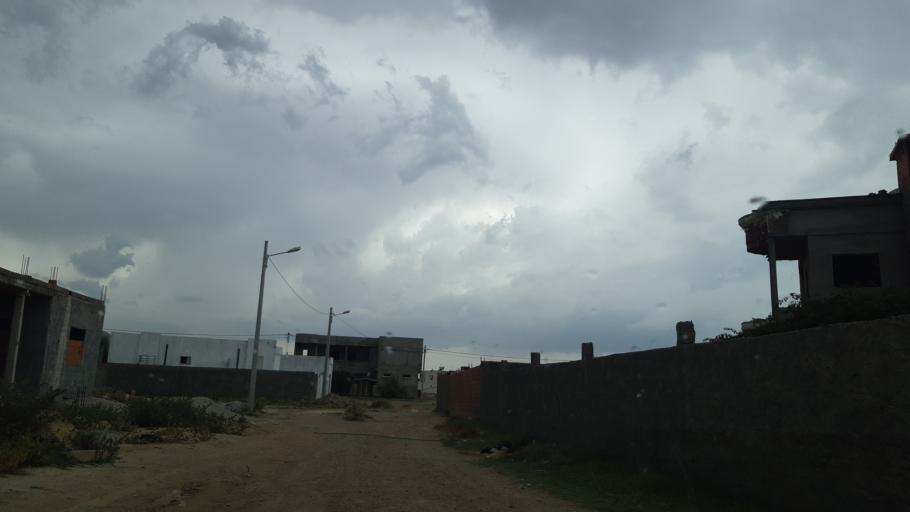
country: TN
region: Al Qayrawan
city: Sbikha
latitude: 36.1238
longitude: 10.0897
